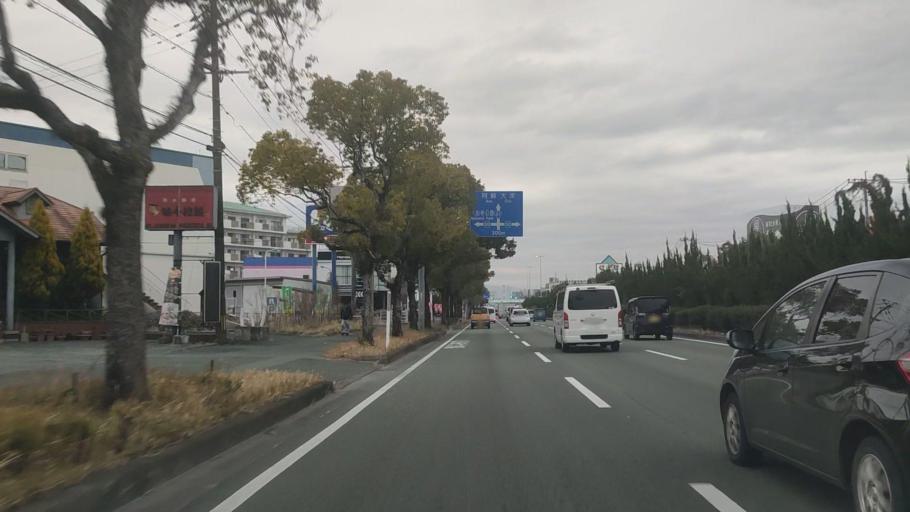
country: JP
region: Kumamoto
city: Kumamoto
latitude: 32.7722
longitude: 130.7321
